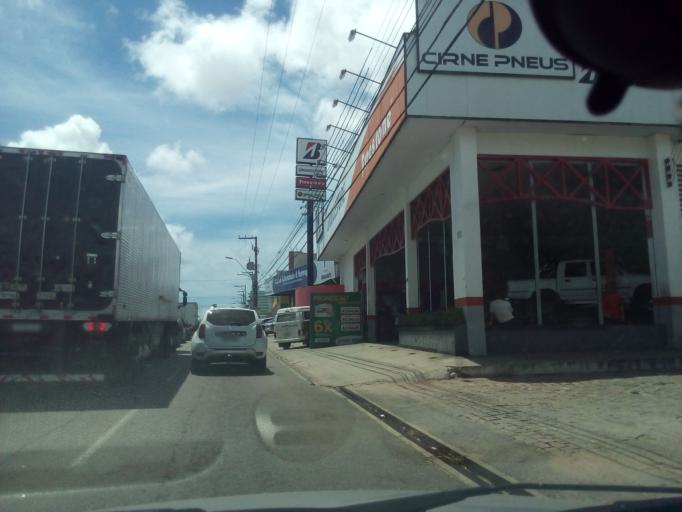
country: BR
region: Rio Grande do Norte
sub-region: Natal
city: Natal
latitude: -5.8025
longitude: -35.2338
